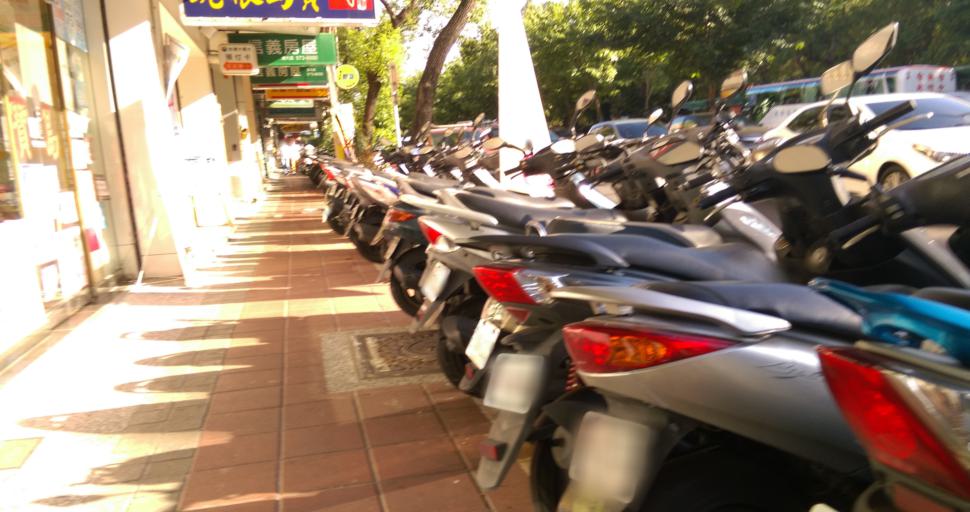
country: TW
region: Taiwan
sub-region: Hsinchu
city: Hsinchu
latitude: 24.7958
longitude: 120.9984
